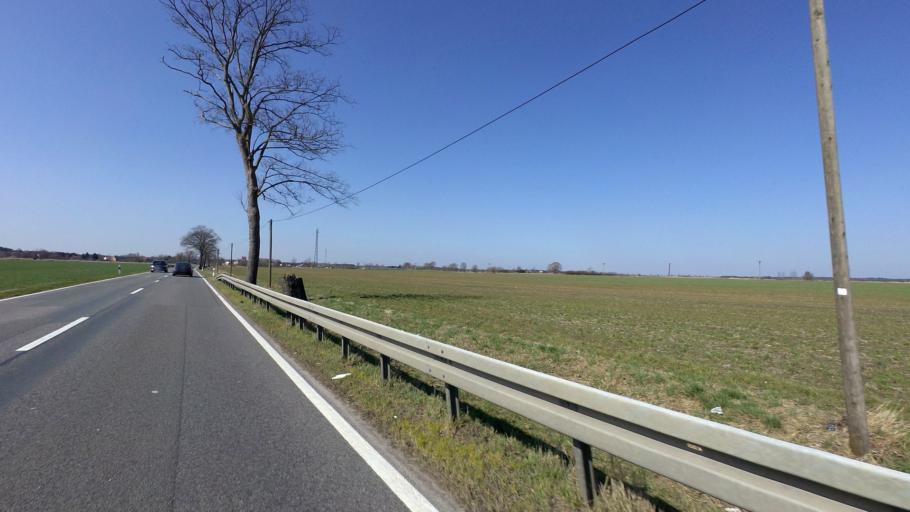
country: DE
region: Brandenburg
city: Ruthnick
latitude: 52.9007
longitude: 12.9884
